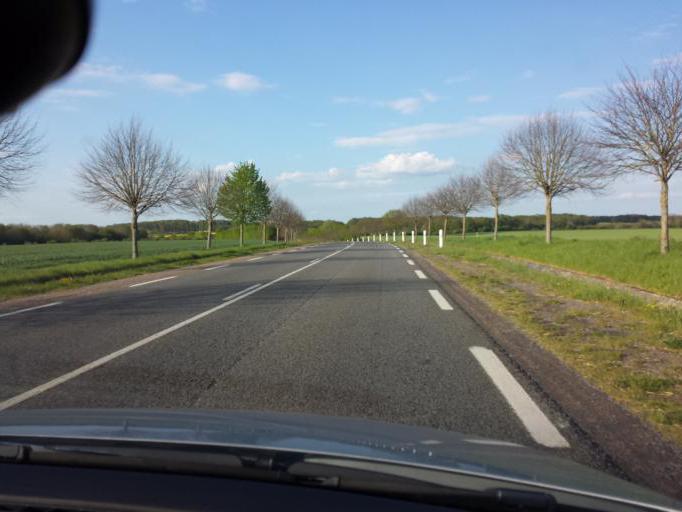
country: FR
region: Haute-Normandie
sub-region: Departement de l'Eure
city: Breteuil
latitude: 48.8305
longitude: 0.9352
